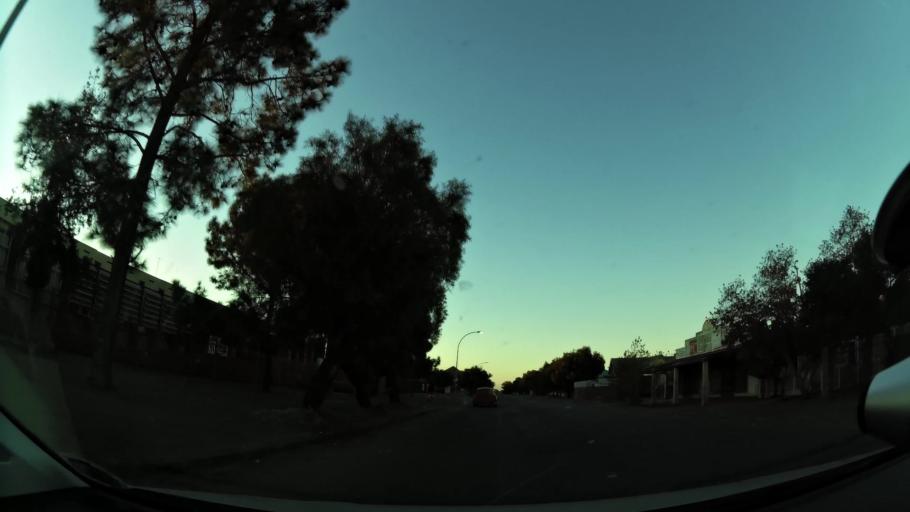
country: ZA
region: Northern Cape
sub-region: Frances Baard District Municipality
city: Kimberley
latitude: -28.7348
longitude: 24.7713
